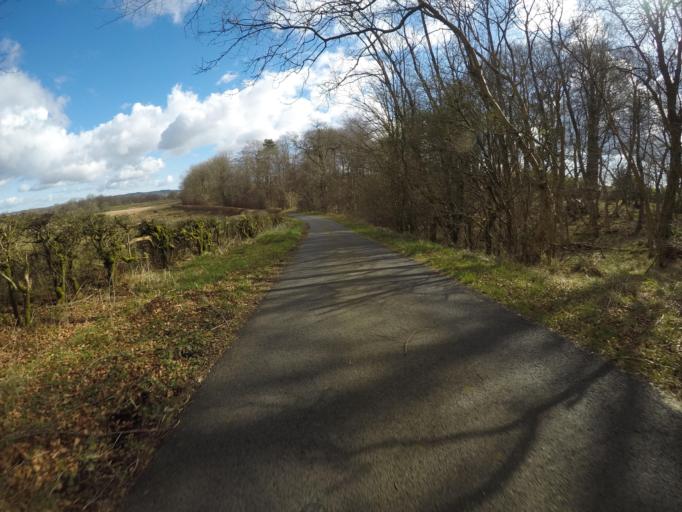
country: GB
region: Scotland
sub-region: North Ayrshire
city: Beith
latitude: 55.7131
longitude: -4.6476
